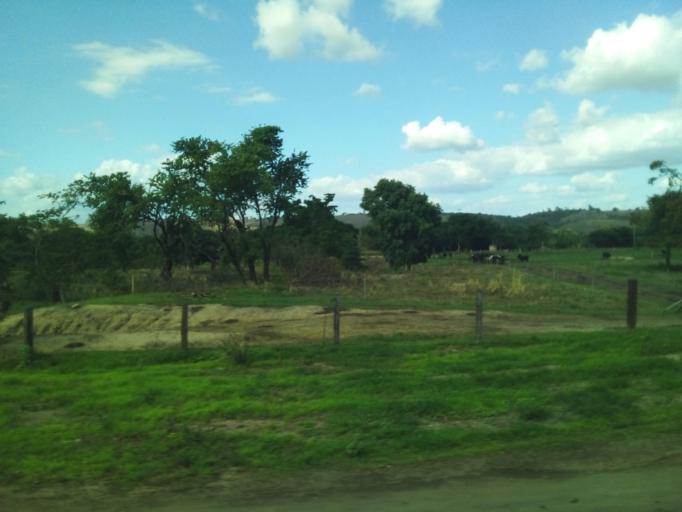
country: BR
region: Minas Gerais
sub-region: Conselheiro Pena
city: Conselheiro Pena
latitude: -18.9950
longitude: -41.5954
